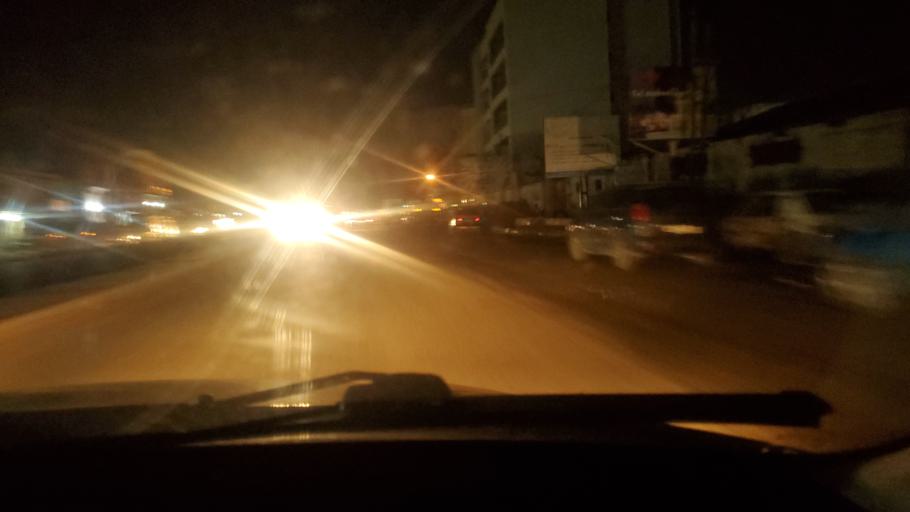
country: SN
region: Dakar
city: Pikine
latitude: 14.7451
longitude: -17.3809
